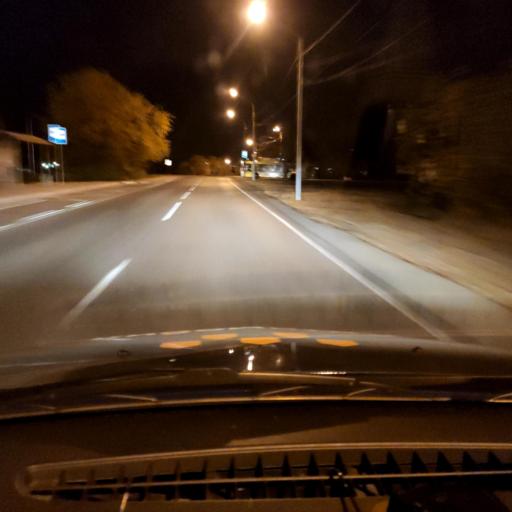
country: RU
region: Voronezj
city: Shilovo
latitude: 51.6045
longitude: 39.0378
